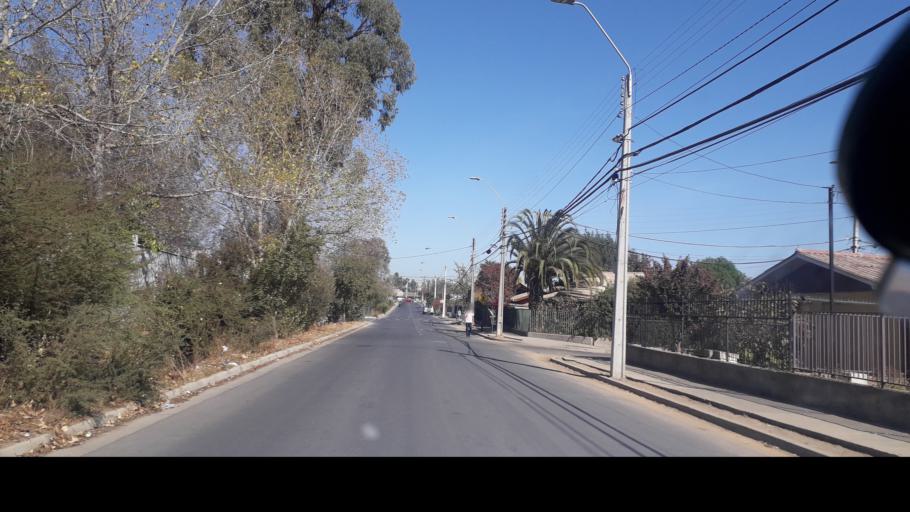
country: CL
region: Valparaiso
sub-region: Provincia de Marga Marga
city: Villa Alemana
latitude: -33.0458
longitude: -71.3492
